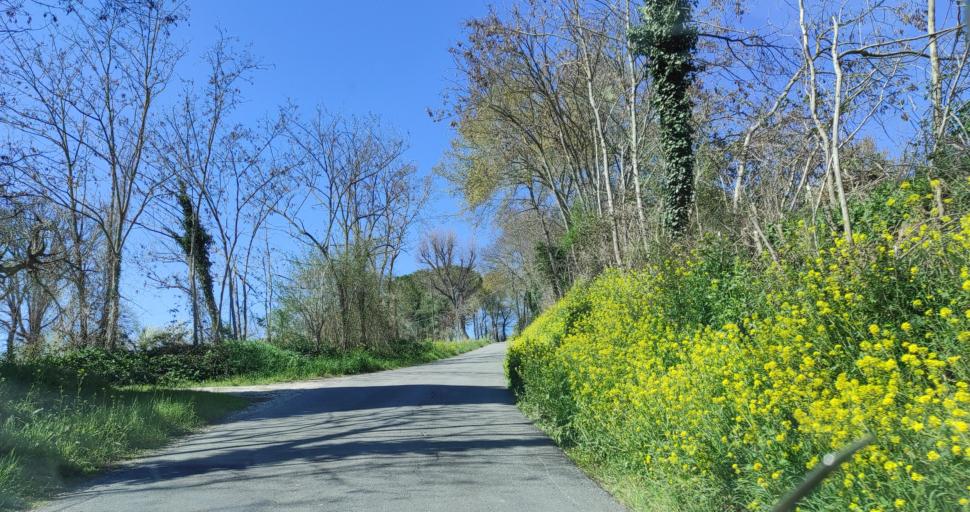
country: IT
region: The Marches
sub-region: Provincia di Macerata
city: Macerata
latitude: 43.3126
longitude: 13.4843
